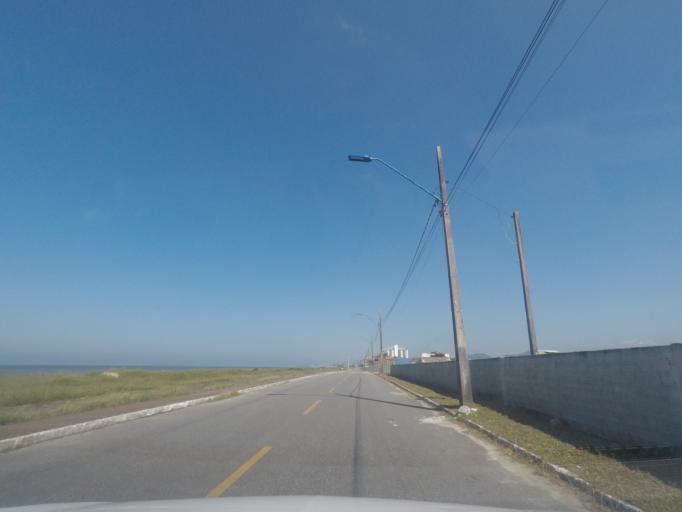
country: BR
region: Parana
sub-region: Pontal Do Parana
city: Pontal do Parana
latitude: -25.7438
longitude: -48.4966
